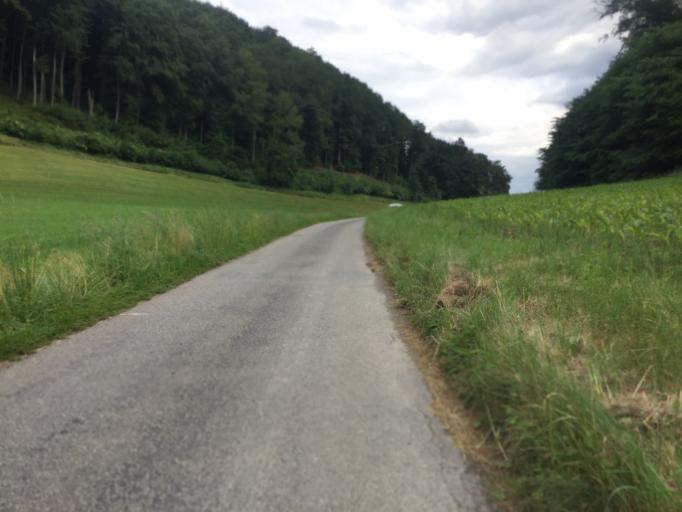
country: CH
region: Bern
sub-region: Bern-Mittelland District
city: Stettlen
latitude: 46.9464
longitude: 7.5095
